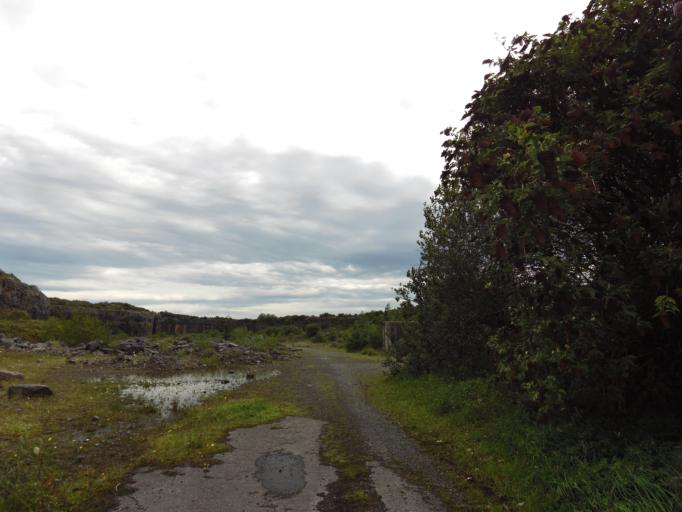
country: IE
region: Connaught
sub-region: County Galway
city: Gaillimh
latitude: 53.3173
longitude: -9.0627
